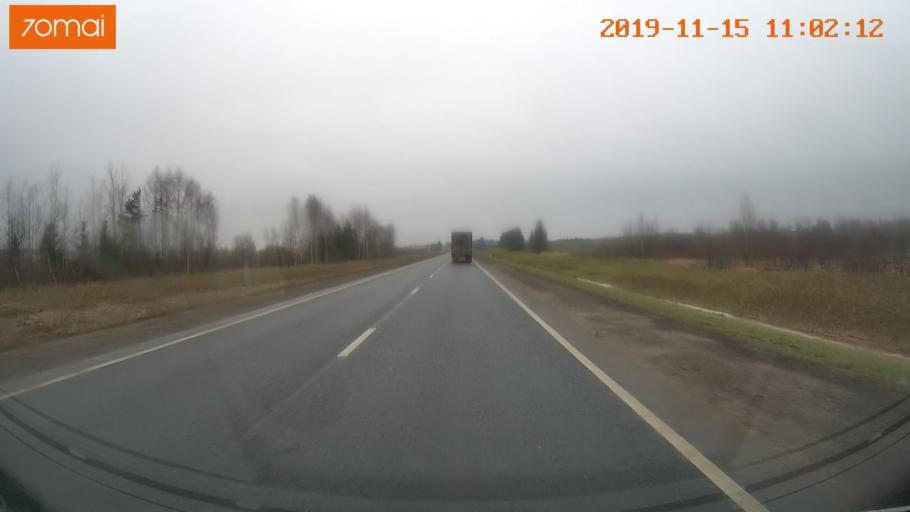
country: RU
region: Vologda
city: Chebsara
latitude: 59.1302
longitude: 38.9335
